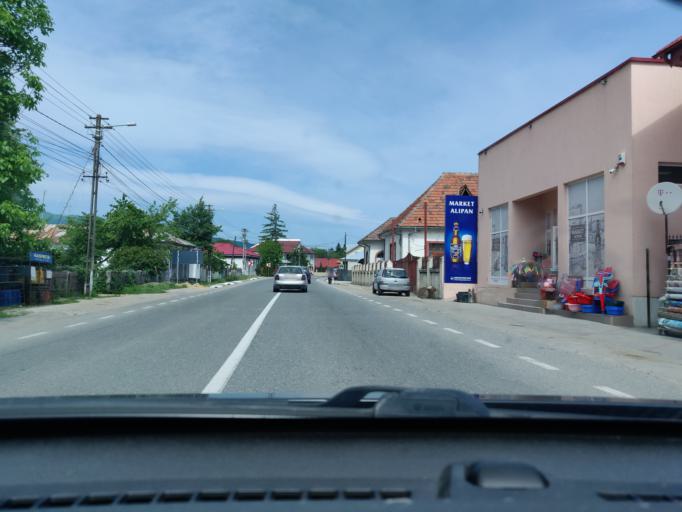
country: RO
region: Vrancea
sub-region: Comuna Bolotesti
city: Bolotesti
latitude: 45.8399
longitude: 27.0729
